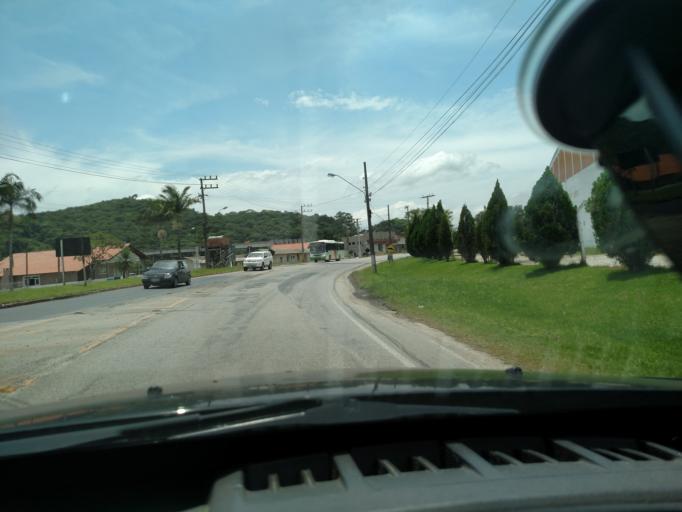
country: BR
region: Santa Catarina
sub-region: Gaspar
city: Gaspar
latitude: -26.9104
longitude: -48.9345
